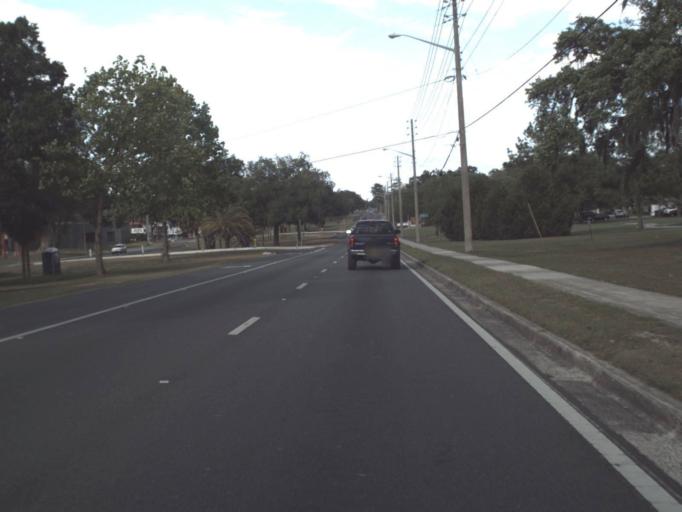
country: US
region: Florida
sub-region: Marion County
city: Ocala
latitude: 29.1915
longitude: -82.0956
